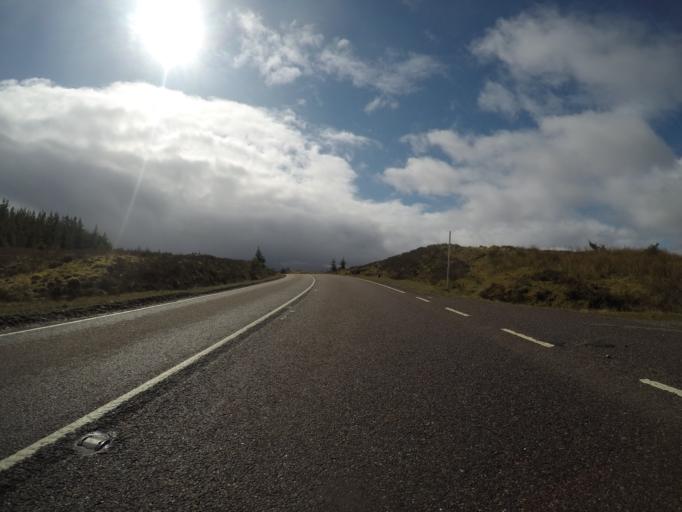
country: GB
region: Scotland
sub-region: Highland
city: Spean Bridge
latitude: 57.0962
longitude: -4.9949
